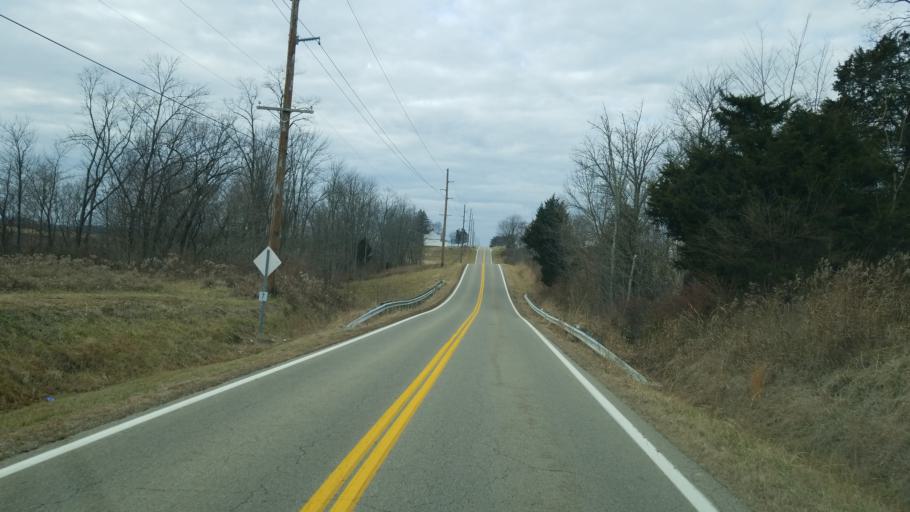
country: US
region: Ohio
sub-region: Ross County
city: Frankfort
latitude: 39.3541
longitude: -83.2473
